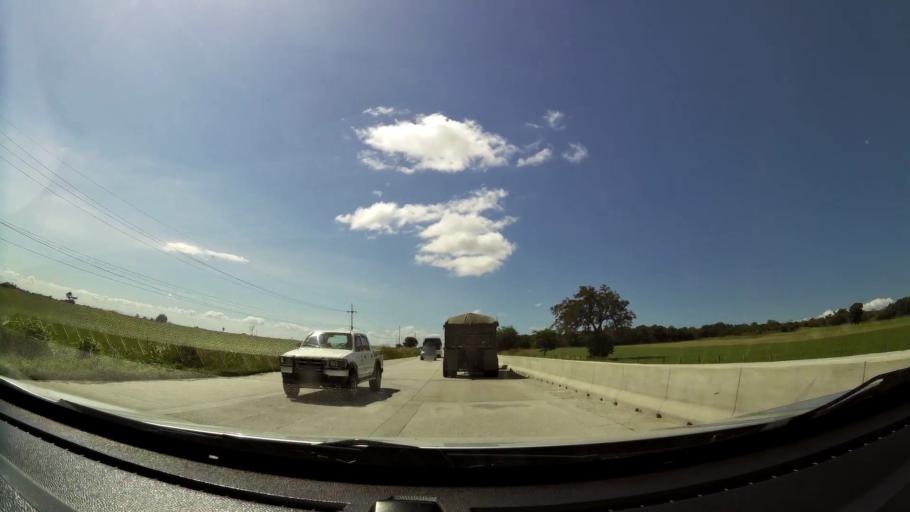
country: CR
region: Guanacaste
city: Bagaces
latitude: 10.5404
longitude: -85.3211
